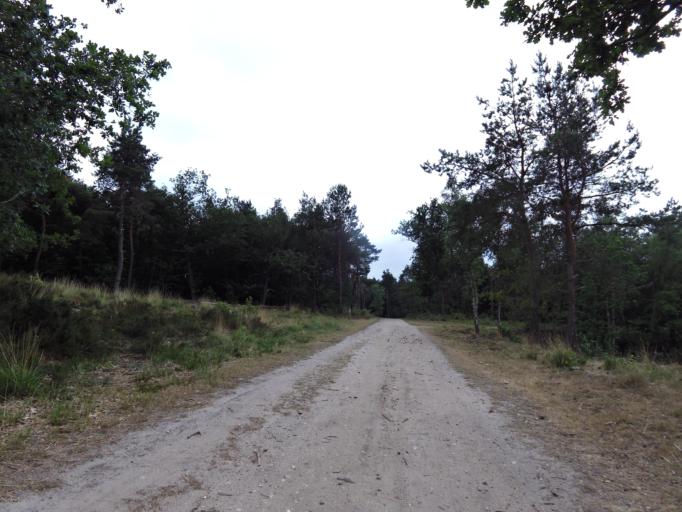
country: NL
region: North Brabant
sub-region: Gemeente Cuijk
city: Cuijk
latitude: 51.7617
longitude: 5.8837
